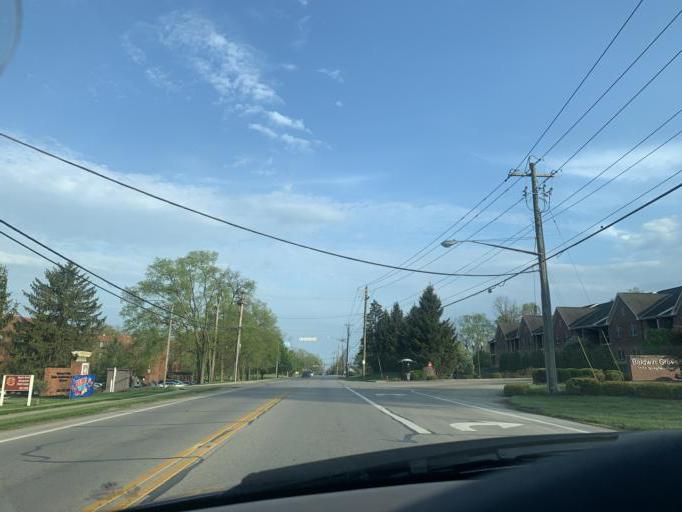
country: US
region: Ohio
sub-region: Hamilton County
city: Springdale
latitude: 39.2763
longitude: -84.4804
